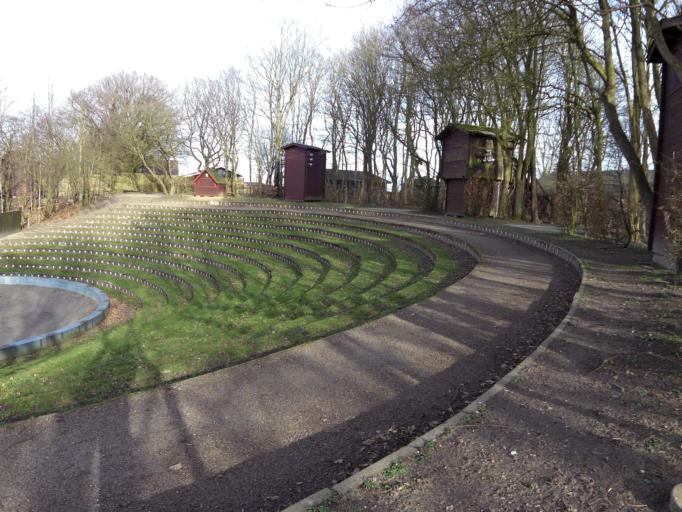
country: DK
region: South Denmark
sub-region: Kolding Kommune
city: Vamdrup
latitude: 55.3596
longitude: 9.2155
